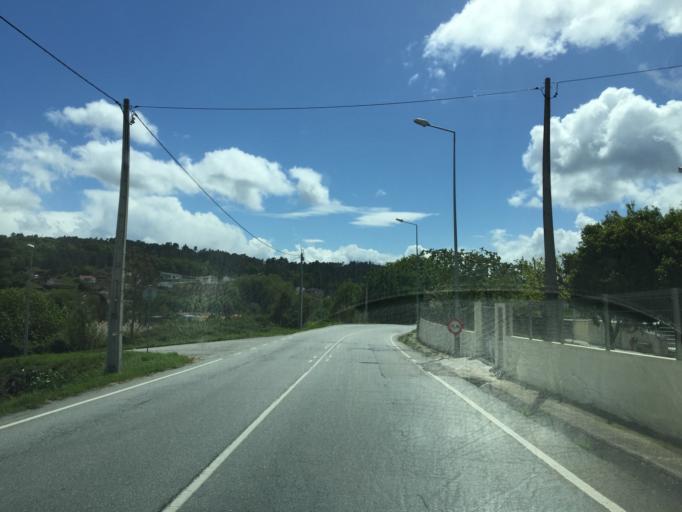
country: PT
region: Viseu
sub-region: Viseu
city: Viseu
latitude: 40.6560
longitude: -7.9390
